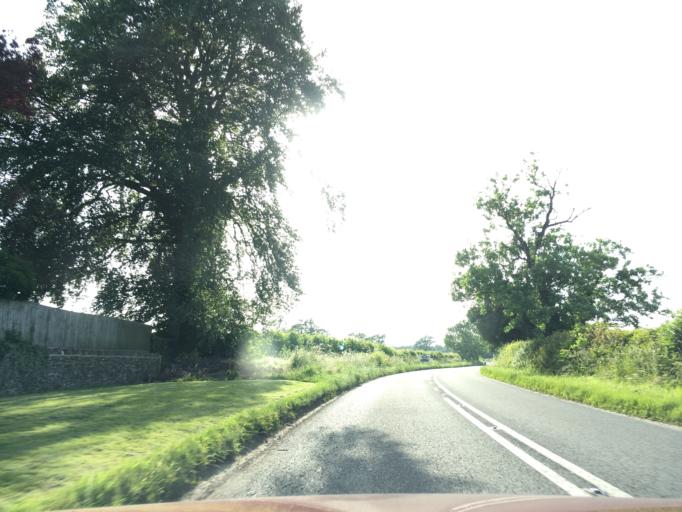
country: GB
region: England
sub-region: Wiltshire
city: Cricklade
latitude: 51.7083
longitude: -1.8633
